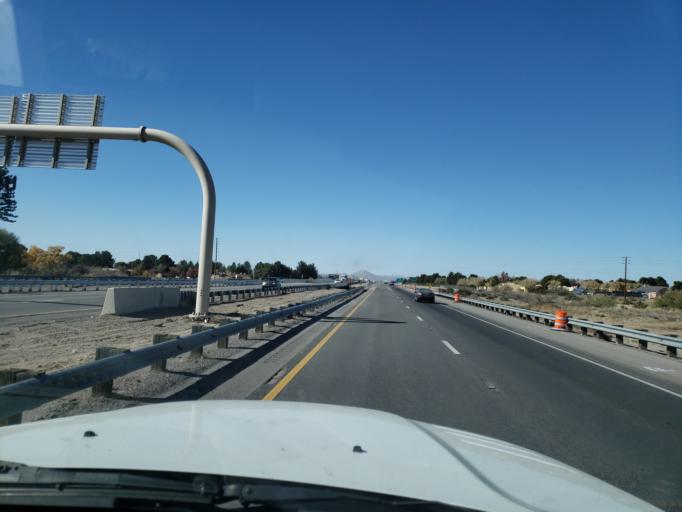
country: US
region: New Mexico
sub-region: Dona Ana County
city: University Park
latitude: 32.2685
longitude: -106.7443
